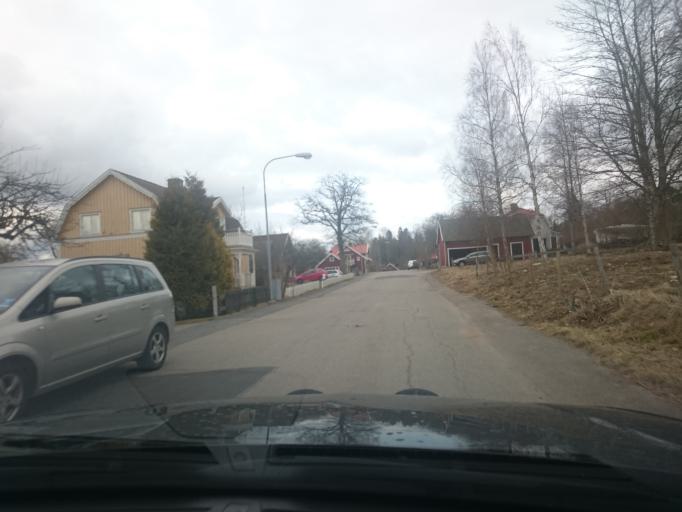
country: SE
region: Joenkoeping
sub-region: Vetlanda Kommun
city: Vetlanda
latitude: 57.2949
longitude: 15.1264
